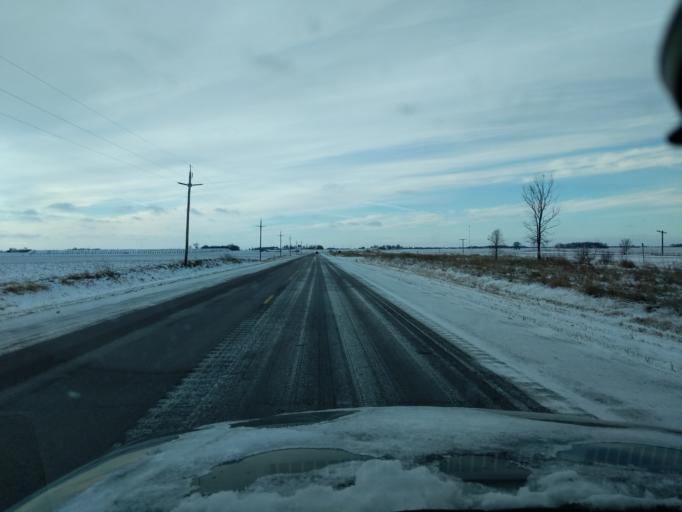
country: US
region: Minnesota
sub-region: Renville County
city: Hector
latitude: 44.7248
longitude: -94.5431
